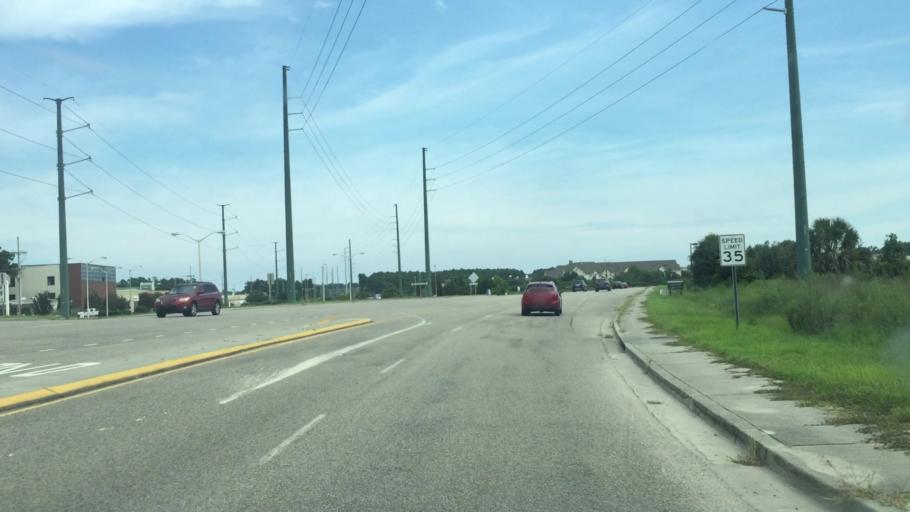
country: US
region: South Carolina
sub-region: Horry County
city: Forestbrook
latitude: 33.7183
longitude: -78.9317
